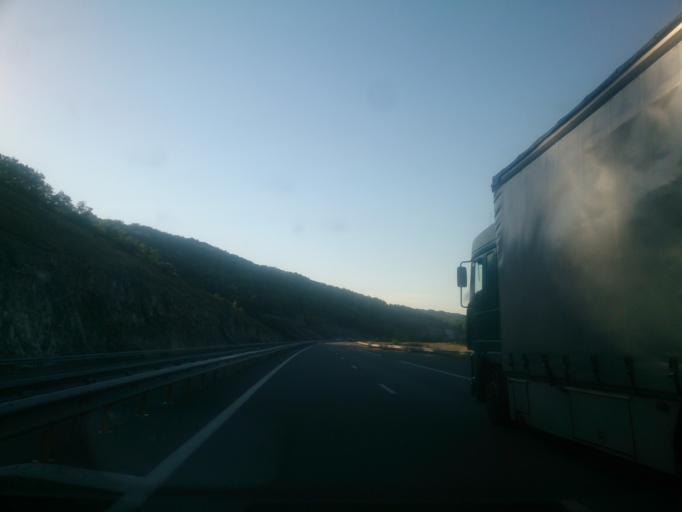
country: FR
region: Midi-Pyrenees
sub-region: Departement du Lot
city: Le Vigan
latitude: 44.7954
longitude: 1.5156
